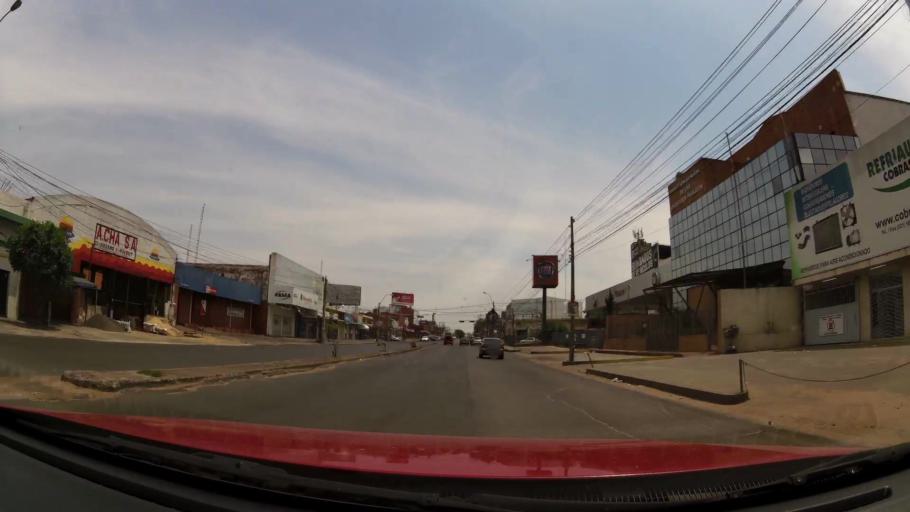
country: PY
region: Central
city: Lambare
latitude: -25.3167
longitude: -57.5731
